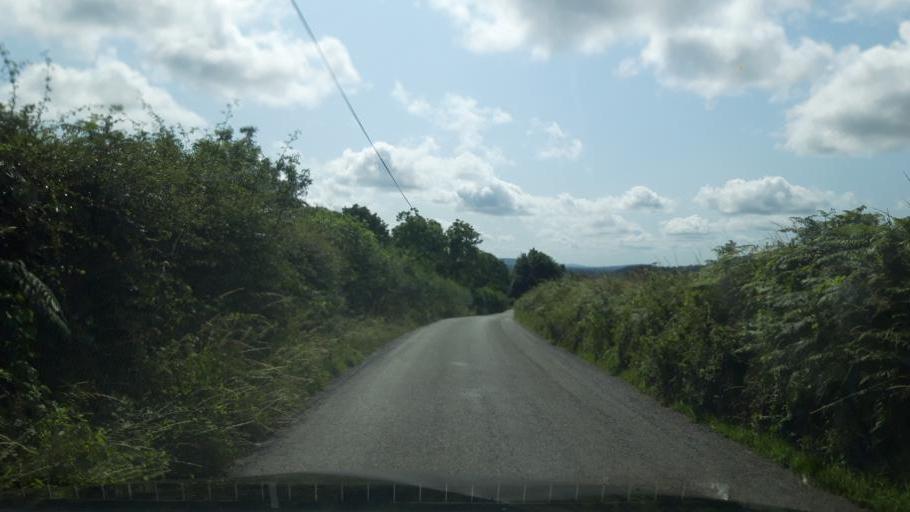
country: IE
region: Leinster
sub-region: Kilkenny
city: Graiguenamanagh
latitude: 52.5567
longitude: -6.9800
